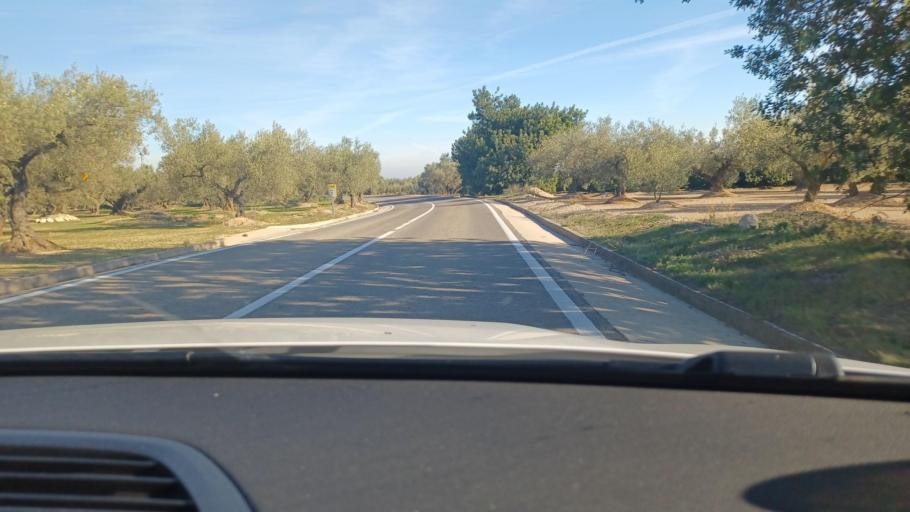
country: ES
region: Catalonia
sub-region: Provincia de Tarragona
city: Mas de Barberans
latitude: 40.7142
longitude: 0.4139
